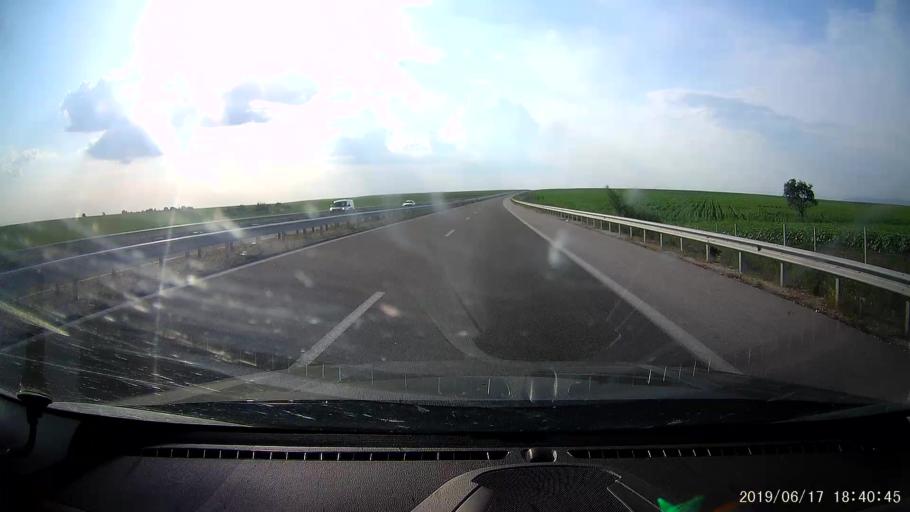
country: BG
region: Stara Zagora
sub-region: Obshtina Chirpan
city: Chirpan
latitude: 42.1599
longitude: 25.2702
